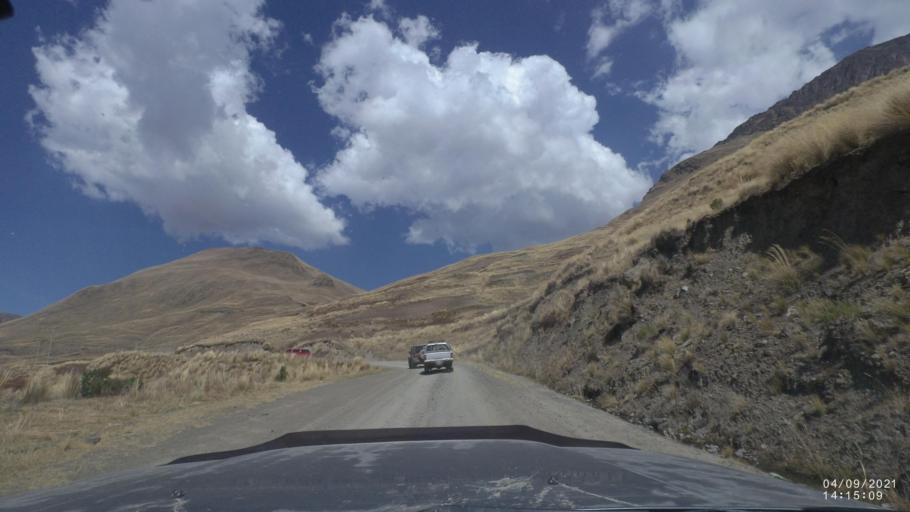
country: BO
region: Cochabamba
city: Sipe Sipe
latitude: -17.2282
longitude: -66.4420
